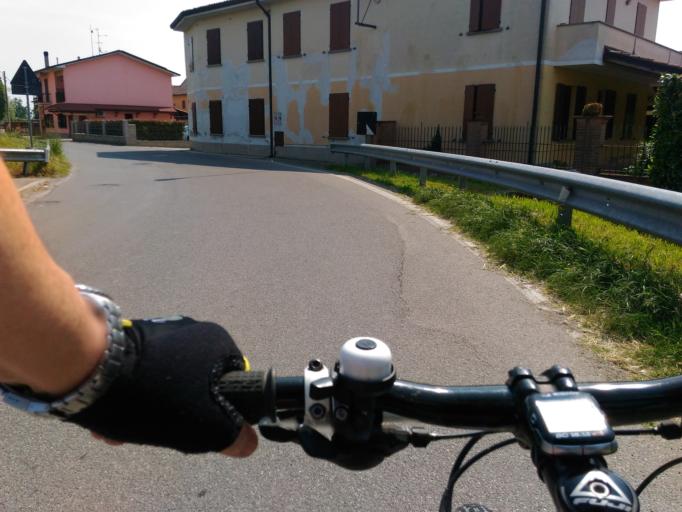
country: IT
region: Lombardy
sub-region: Provincia di Lodi
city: Bargano
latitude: 45.2413
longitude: 9.4452
